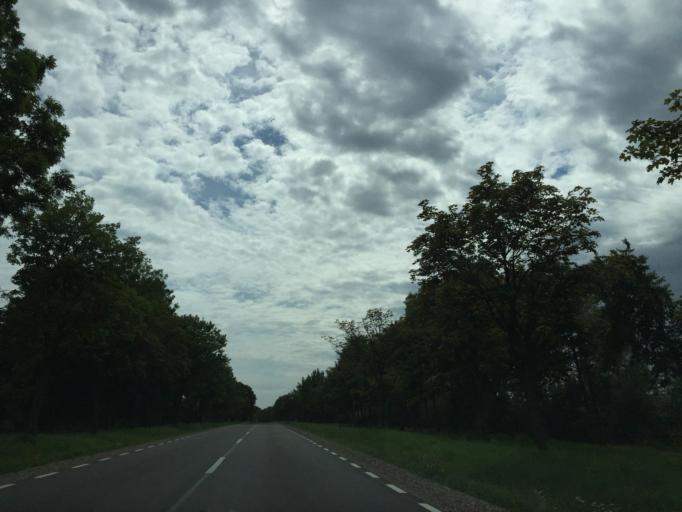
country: PL
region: Podlasie
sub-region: Powiat bielski
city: Bocki
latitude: 52.6886
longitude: 23.1172
